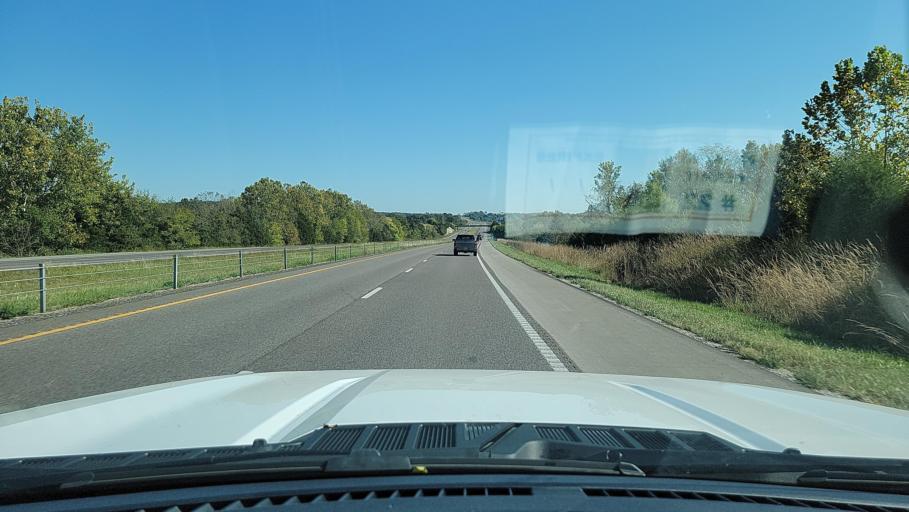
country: US
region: Missouri
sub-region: Sainte Genevieve County
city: Sainte Genevieve
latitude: 37.9551
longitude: -90.1561
